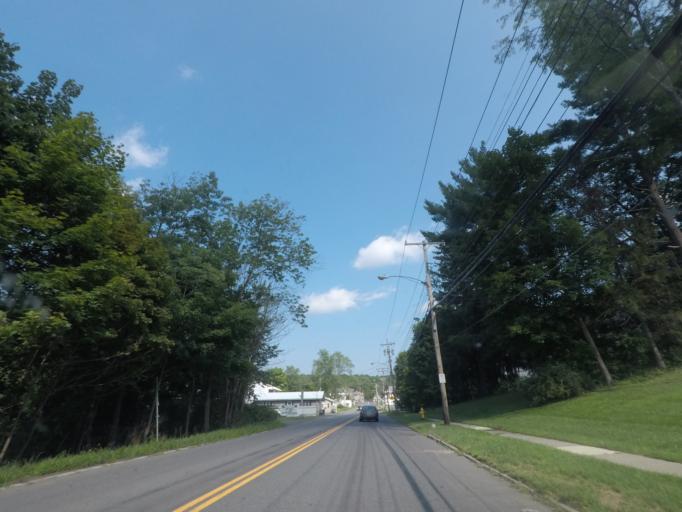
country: US
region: New York
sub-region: Rensselaer County
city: Nassau
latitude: 42.5168
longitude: -73.6138
